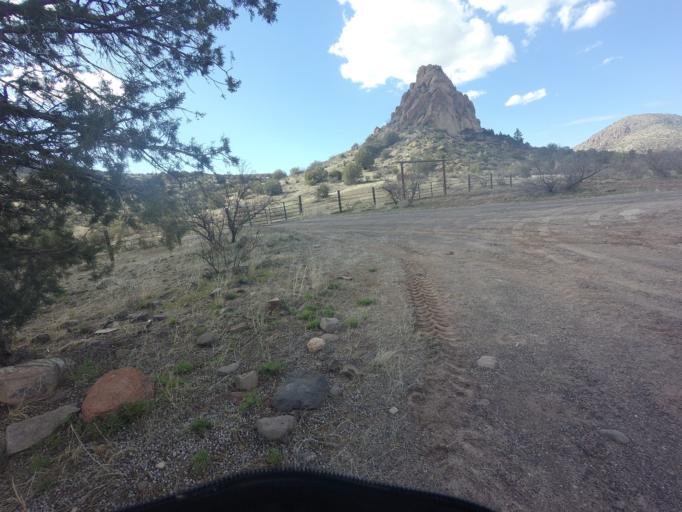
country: US
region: Arizona
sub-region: Yavapai County
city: Camp Verde
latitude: 34.4348
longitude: -111.6873
